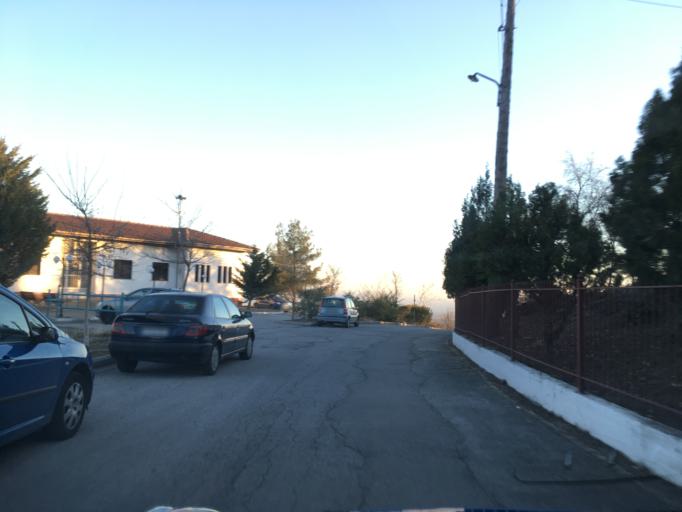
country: GR
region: West Macedonia
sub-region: Nomos Kozanis
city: Koila
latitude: 40.3231
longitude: 21.8222
